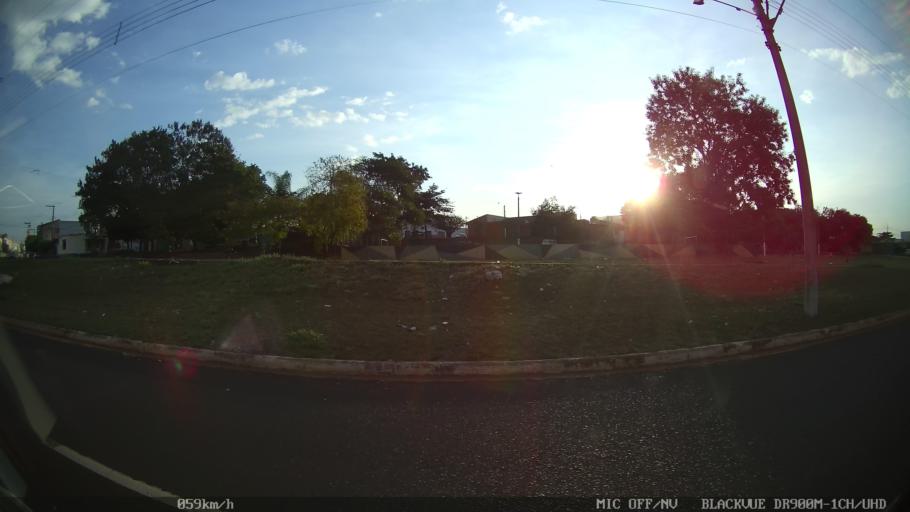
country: BR
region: Sao Paulo
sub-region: Ribeirao Preto
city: Ribeirao Preto
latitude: -21.1313
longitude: -47.8040
